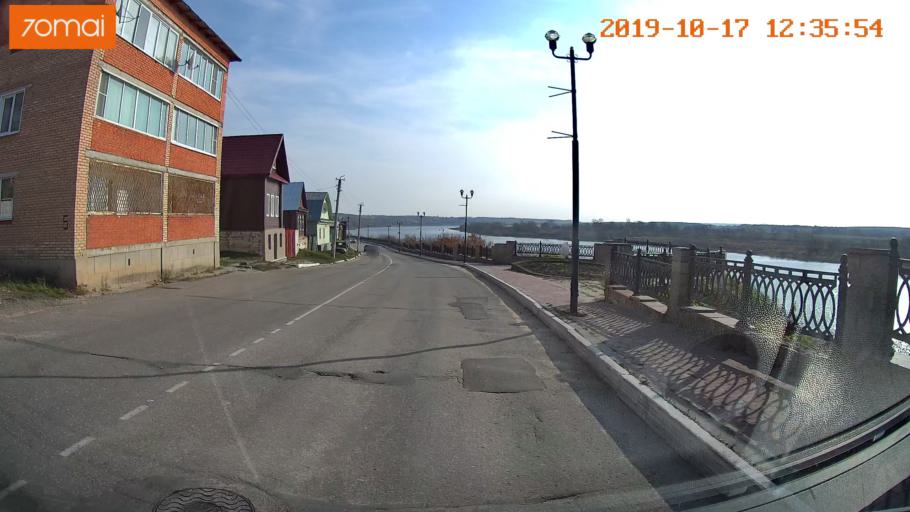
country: RU
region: Rjazan
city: Kasimov
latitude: 54.9415
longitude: 41.3714
